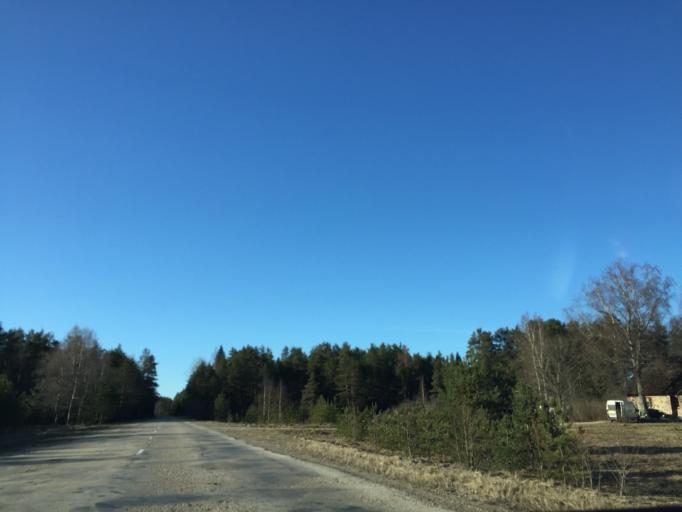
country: LV
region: Ropazu
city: Ropazi
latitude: 56.9440
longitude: 24.6015
